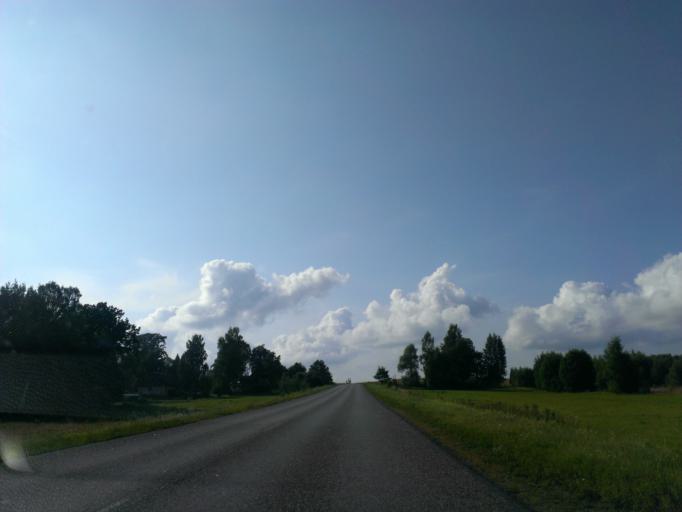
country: LV
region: Priekuli
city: Priekuli
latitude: 57.2972
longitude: 25.4201
